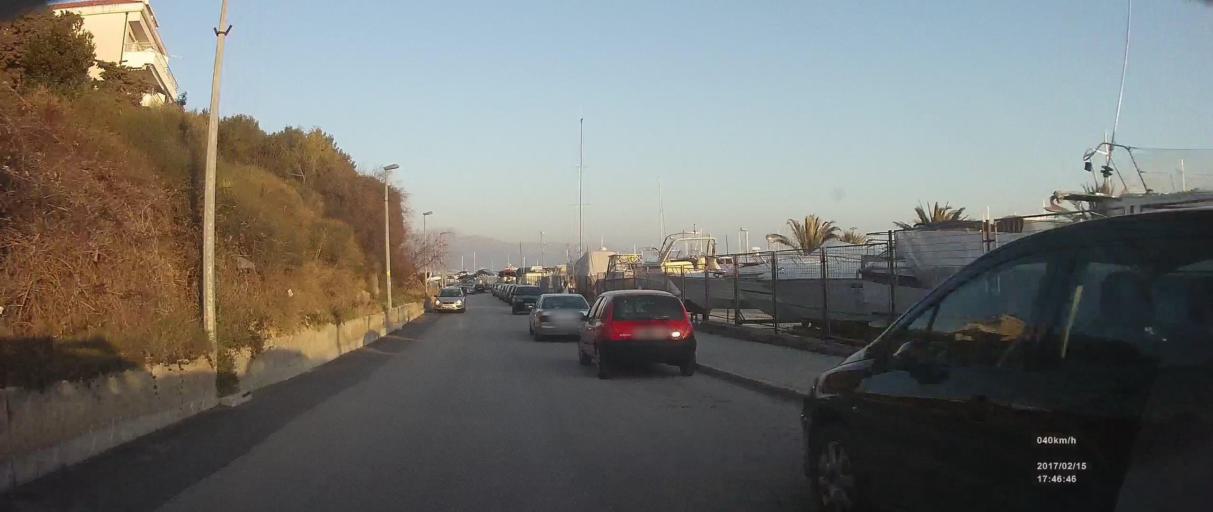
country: HR
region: Splitsko-Dalmatinska
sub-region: Grad Split
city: Split
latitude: 43.5010
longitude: 16.4596
